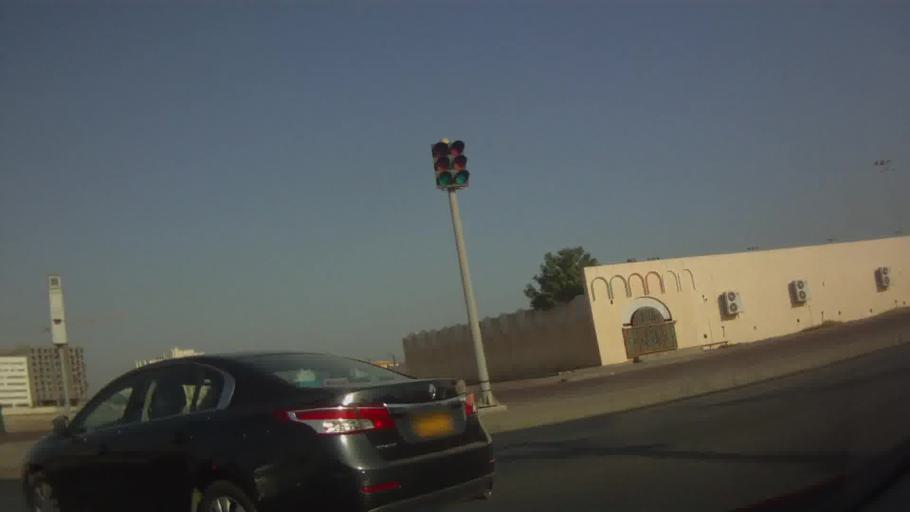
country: OM
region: Muhafazat Masqat
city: Bawshar
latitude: 23.5917
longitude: 58.4174
